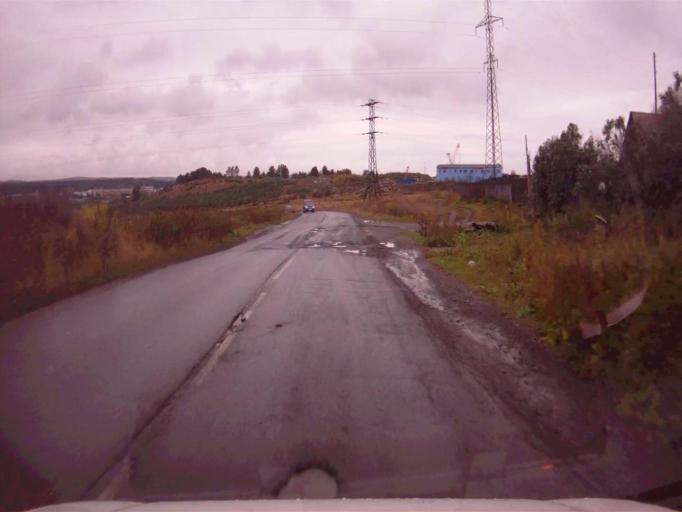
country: RU
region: Chelyabinsk
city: Verkhniy Ufaley
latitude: 56.0604
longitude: 60.1993
